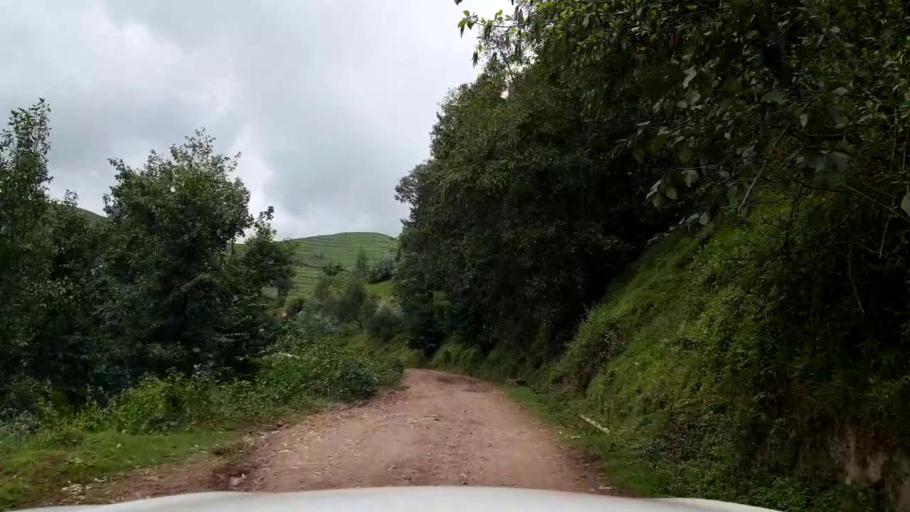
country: RW
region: Western Province
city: Gisenyi
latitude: -1.6494
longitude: 29.4128
